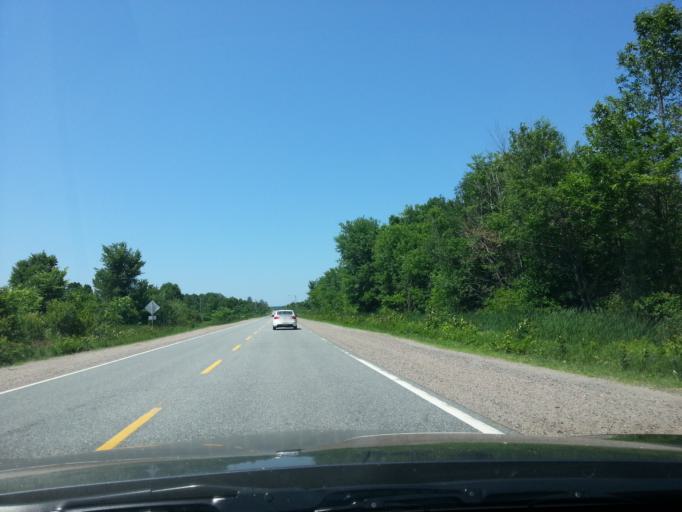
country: CA
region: Ontario
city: Arnprior
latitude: 45.5276
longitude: -76.2205
